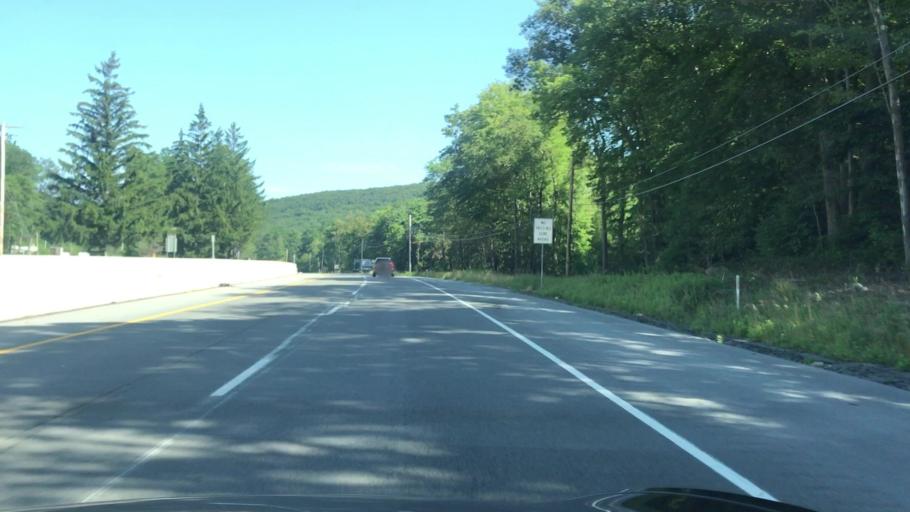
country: US
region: Pennsylvania
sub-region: Lycoming County
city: Montoursville
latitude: 41.2083
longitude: -76.9208
